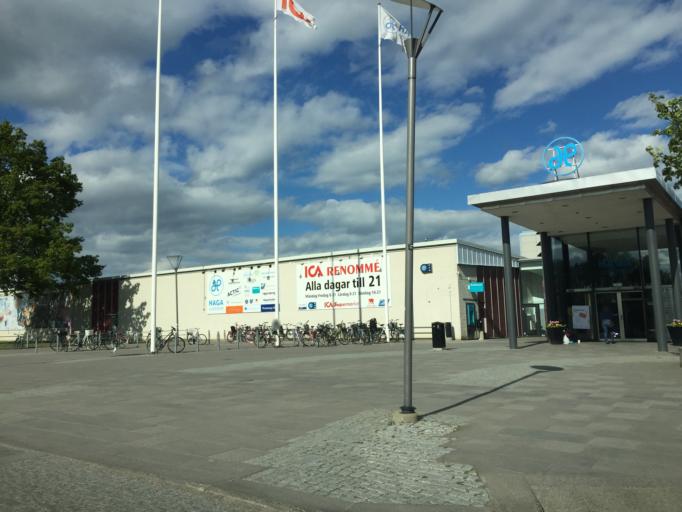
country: SE
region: OErebro
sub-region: Orebro Kommun
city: Orebro
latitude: 59.2753
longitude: 15.1640
